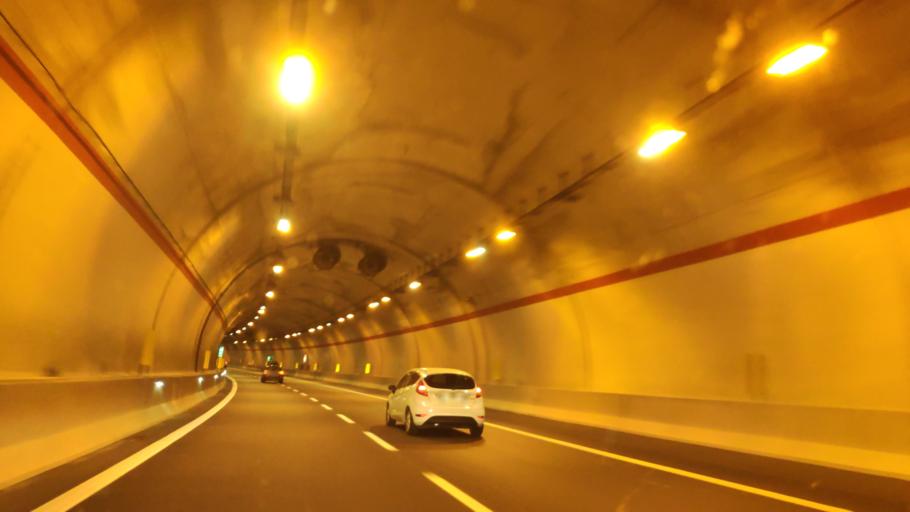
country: IT
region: Calabria
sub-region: Provincia di Cosenza
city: Laino Borgo
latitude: 39.9450
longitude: 15.9590
